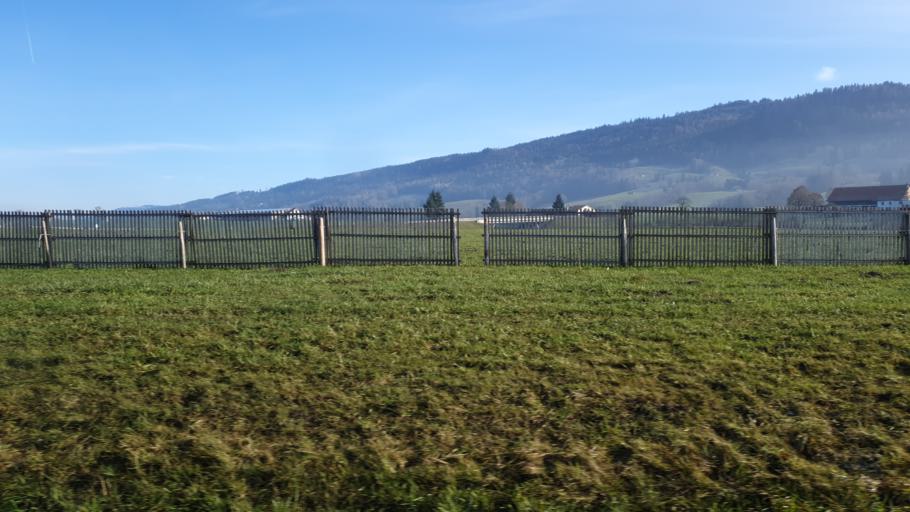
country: CH
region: Fribourg
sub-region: Veveyse District
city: Chatel-Saint-Denis
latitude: 46.5858
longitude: 6.9246
